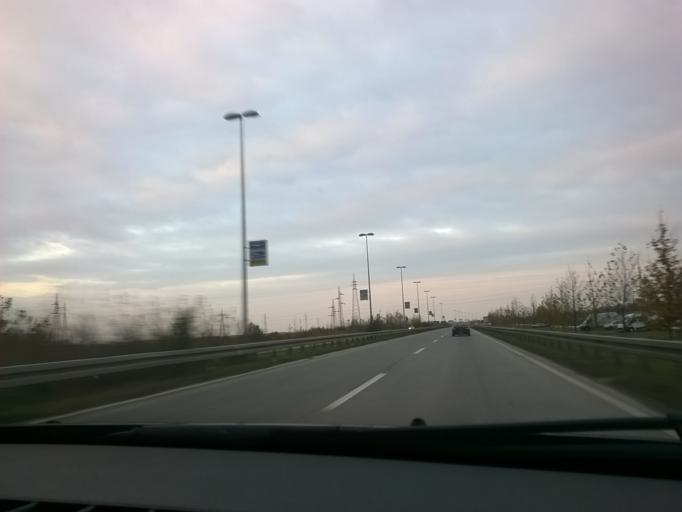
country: RS
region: Autonomna Pokrajina Vojvodina
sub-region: Juznobacki Okrug
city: Novi Sad
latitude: 45.2899
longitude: 19.8529
